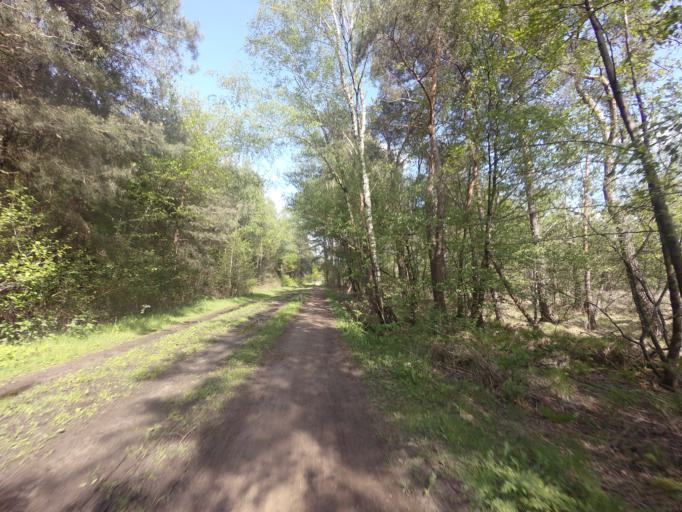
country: NL
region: Overijssel
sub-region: Gemeente Haaksbergen
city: Haaksbergen
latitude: 52.1627
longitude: 6.7844
